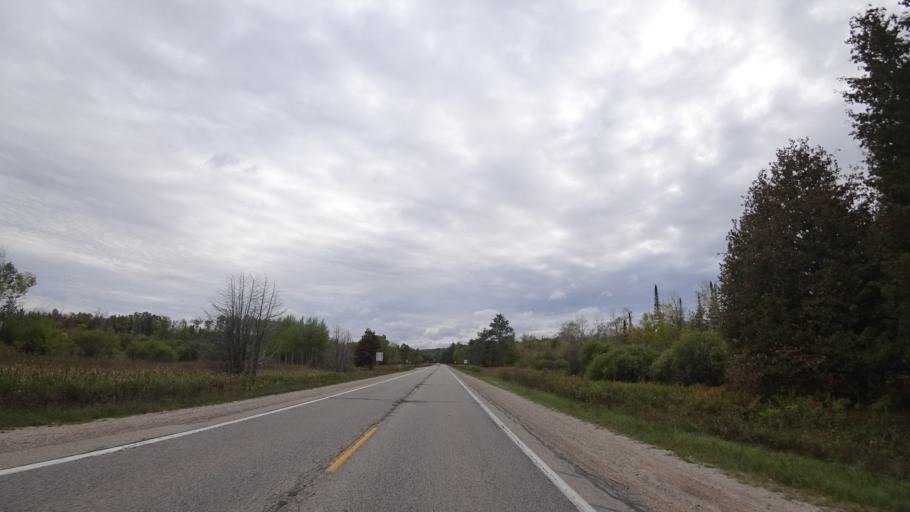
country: US
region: Michigan
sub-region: Charlevoix County
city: Boyne City
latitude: 45.2201
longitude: -84.9227
